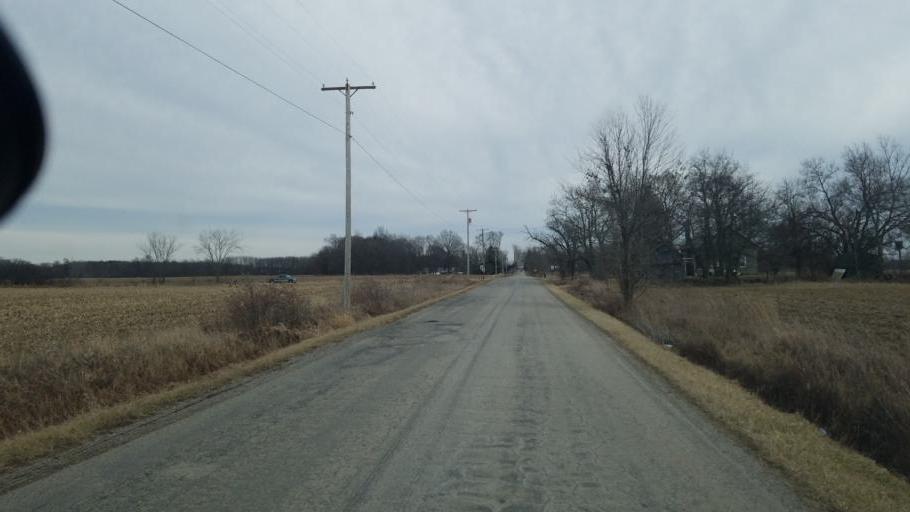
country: US
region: Ohio
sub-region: Delaware County
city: Ashley
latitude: 40.4561
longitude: -83.0108
